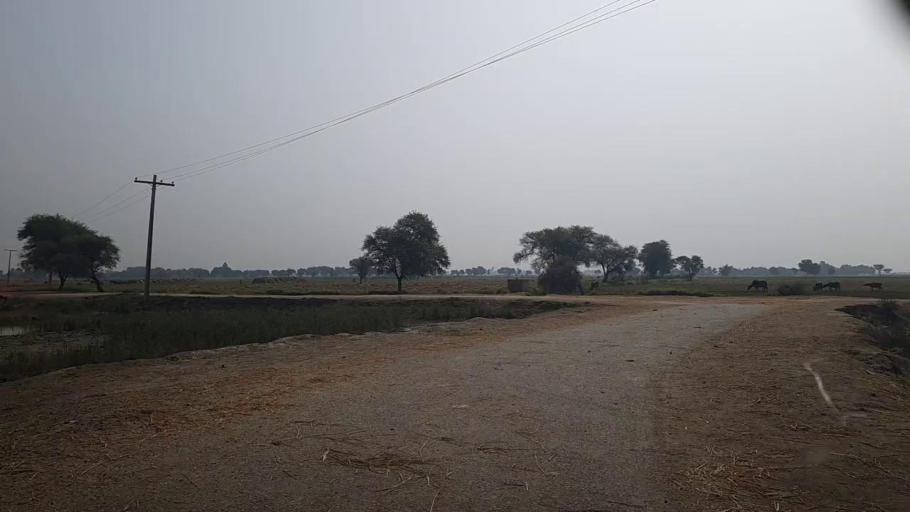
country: PK
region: Sindh
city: Kashmor
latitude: 28.3799
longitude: 69.4384
